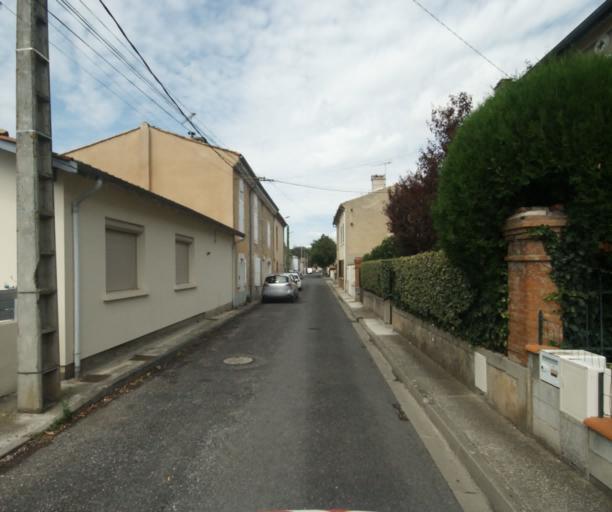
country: FR
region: Midi-Pyrenees
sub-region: Departement de la Haute-Garonne
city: Revel
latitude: 43.4615
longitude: 2.0029
